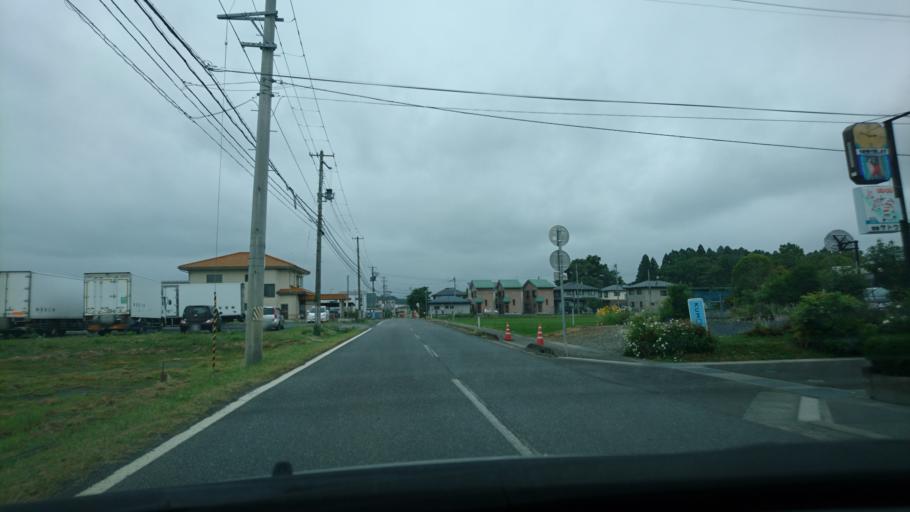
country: JP
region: Iwate
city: Ichinoseki
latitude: 38.9377
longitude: 141.0923
